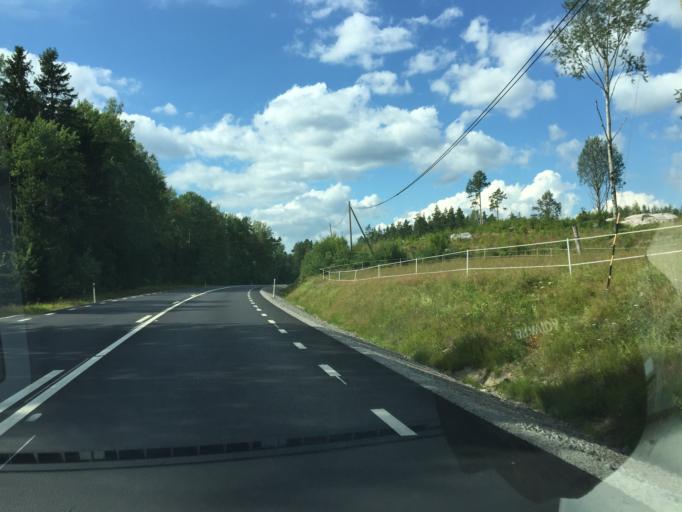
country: SE
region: Gaevleborg
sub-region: Bollnas Kommun
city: Kilafors
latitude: 61.1727
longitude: 16.8009
